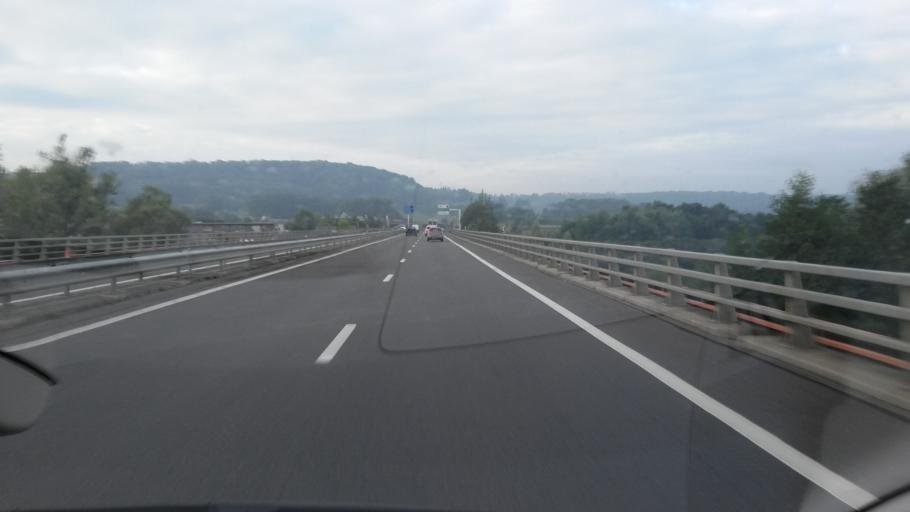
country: FR
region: Champagne-Ardenne
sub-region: Departement des Ardennes
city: La Francheville
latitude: 49.6478
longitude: 4.6315
